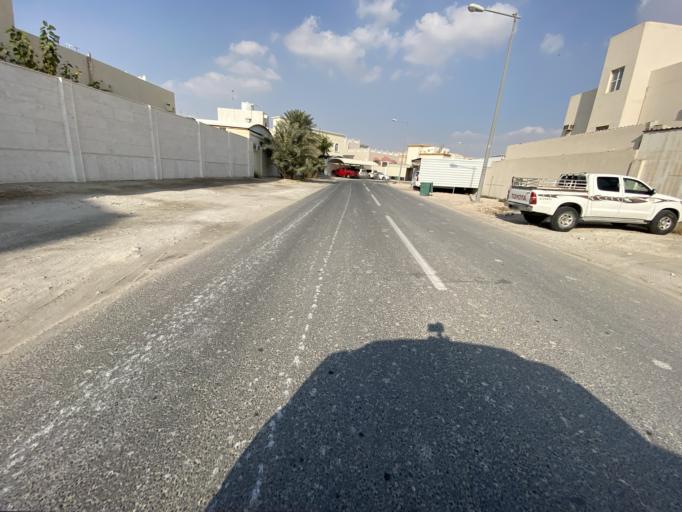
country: QA
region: Baladiyat ar Rayyan
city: Ar Rayyan
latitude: 25.2350
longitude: 51.3758
